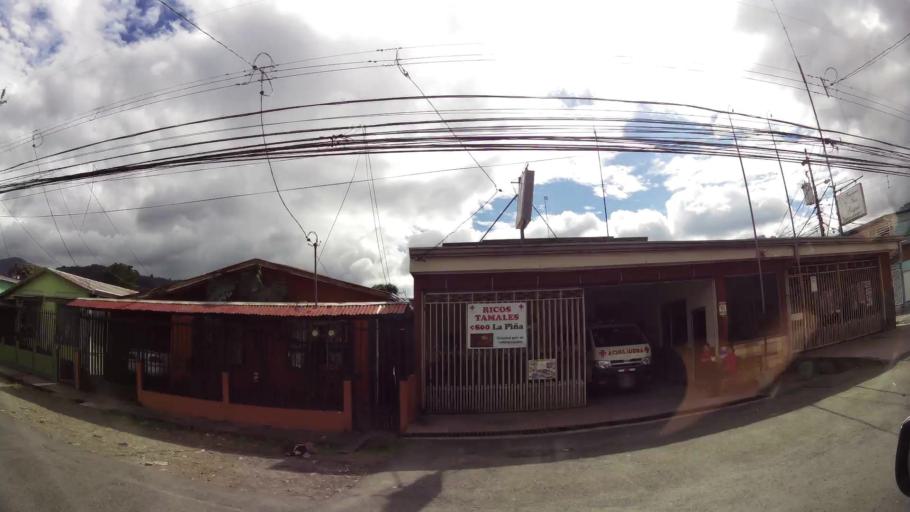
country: CR
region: San Jose
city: San Rafael Arriba
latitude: 9.8776
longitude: -84.0801
